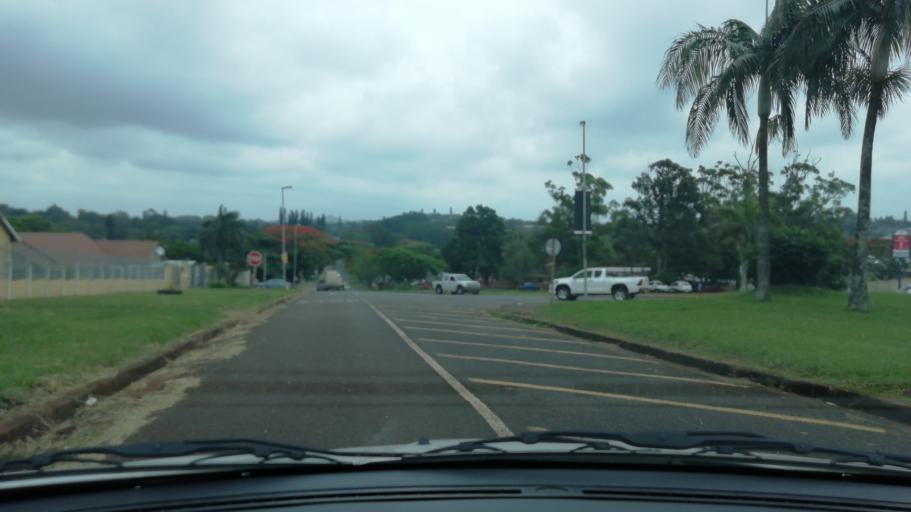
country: ZA
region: KwaZulu-Natal
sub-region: uThungulu District Municipality
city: Empangeni
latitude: -28.7595
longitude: 31.9017
